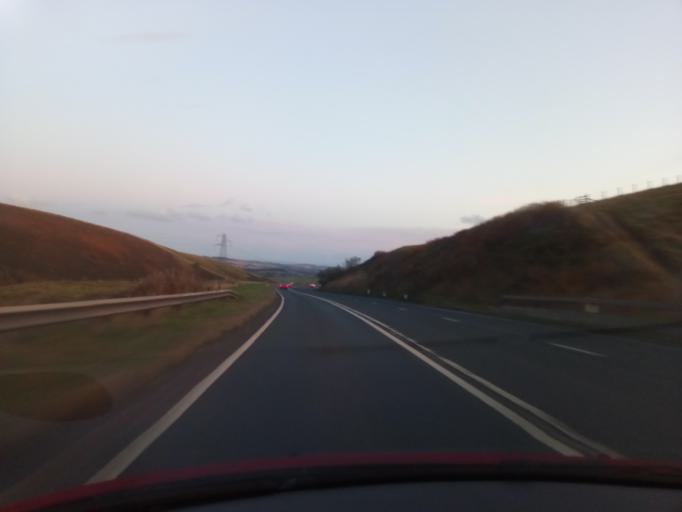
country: GB
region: Scotland
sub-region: The Scottish Borders
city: Lauder
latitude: 55.7980
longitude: -2.8372
